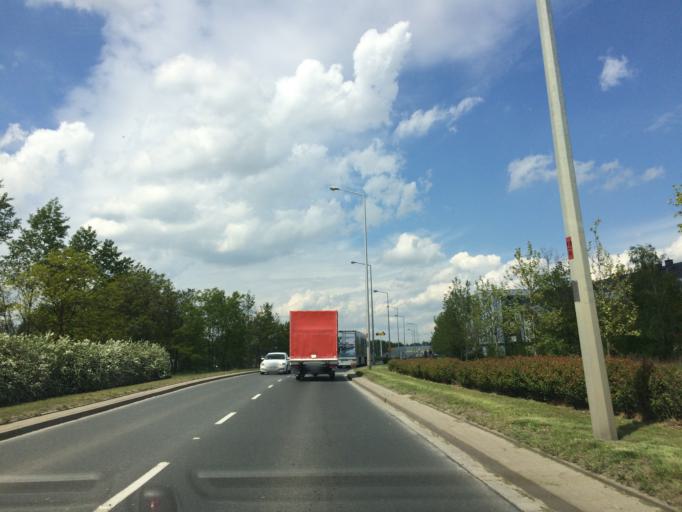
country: PL
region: Lower Silesian Voivodeship
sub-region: Powiat wroclawski
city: Smolec
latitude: 51.1536
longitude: 16.9251
